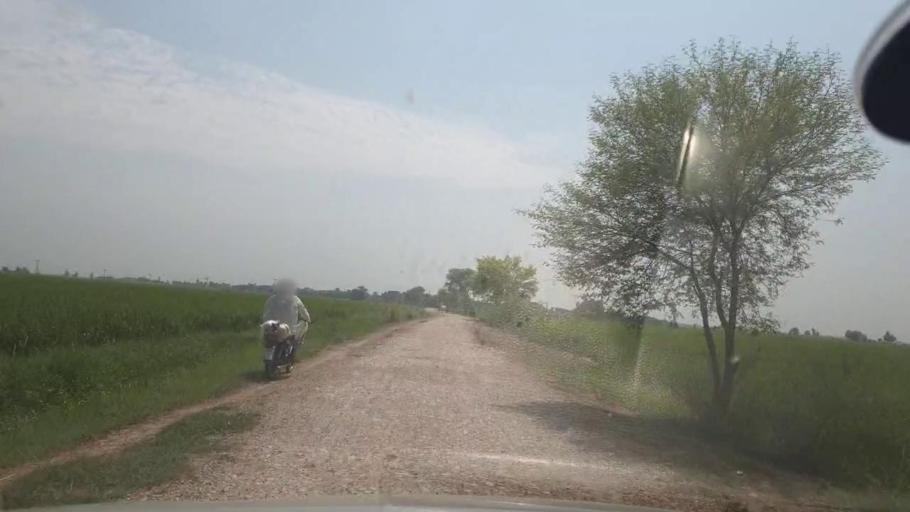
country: PK
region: Sindh
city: Thul
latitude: 28.1647
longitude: 68.6508
